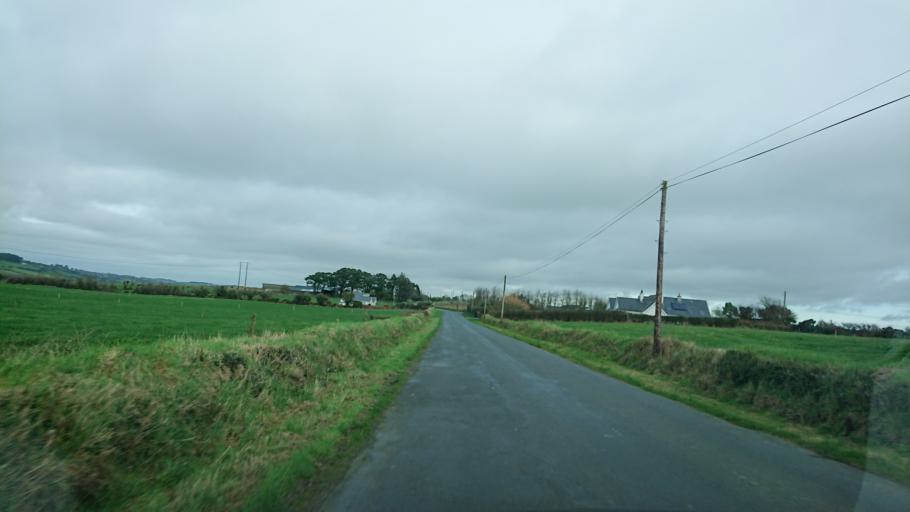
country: IE
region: Munster
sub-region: Waterford
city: Portlaw
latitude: 52.1834
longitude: -7.2981
